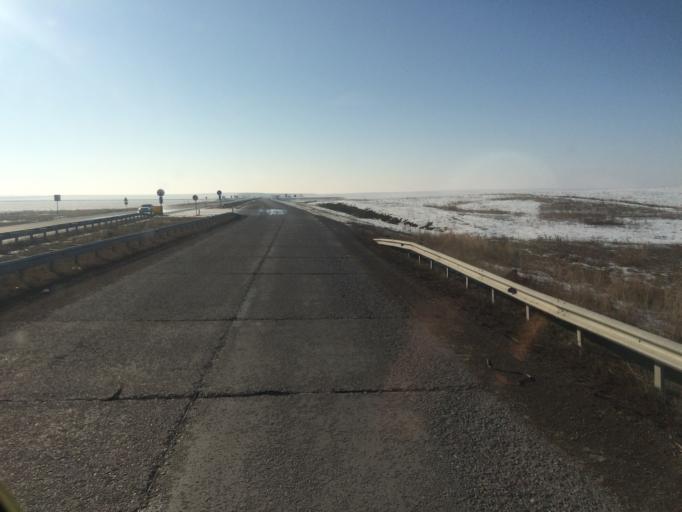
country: KG
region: Chuy
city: Kara-Balta
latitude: 43.1629
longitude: 73.8664
